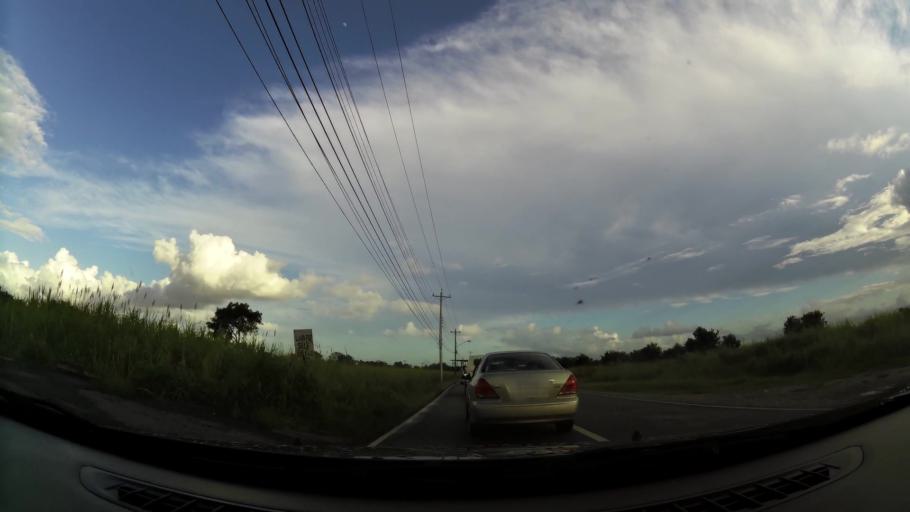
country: TT
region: Tunapuna/Piarco
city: Tunapuna
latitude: 10.5976
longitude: -61.3698
